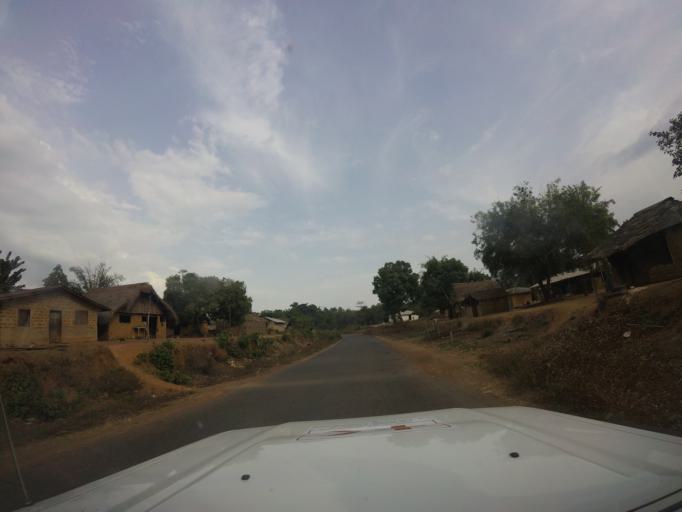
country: LR
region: Grand Cape Mount
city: Robertsport
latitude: 6.9033
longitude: -11.2361
